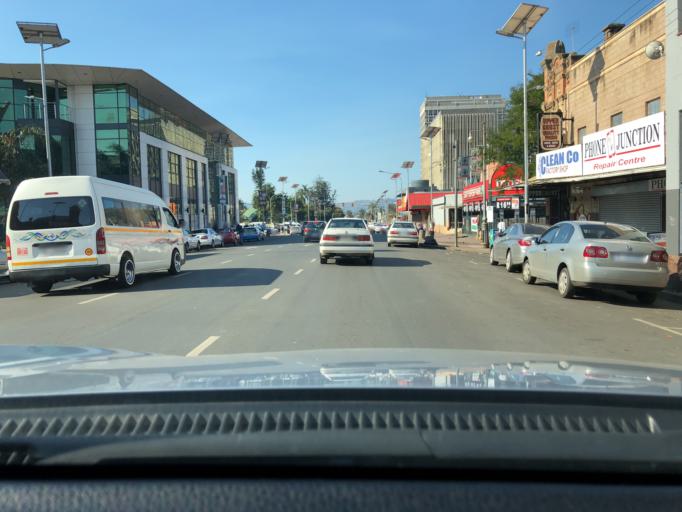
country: ZA
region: KwaZulu-Natal
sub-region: uMgungundlovu District Municipality
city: Pietermaritzburg
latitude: -29.6025
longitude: 30.3806
